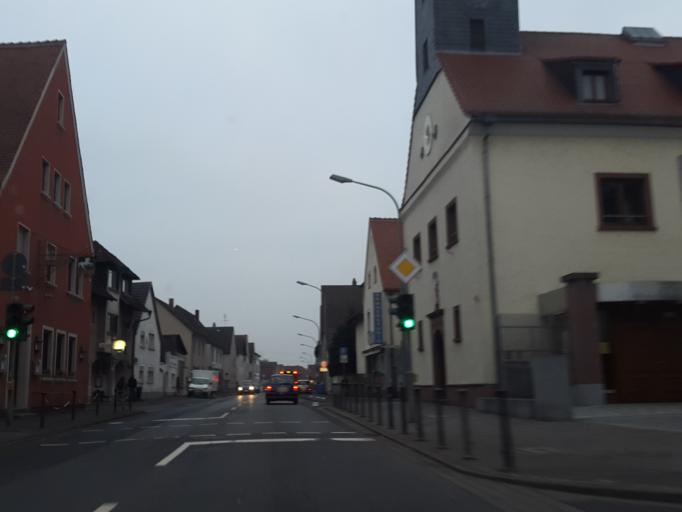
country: DE
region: Bavaria
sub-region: Regierungsbezirk Unterfranken
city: Kleinostheim
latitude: 50.0004
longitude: 9.0615
